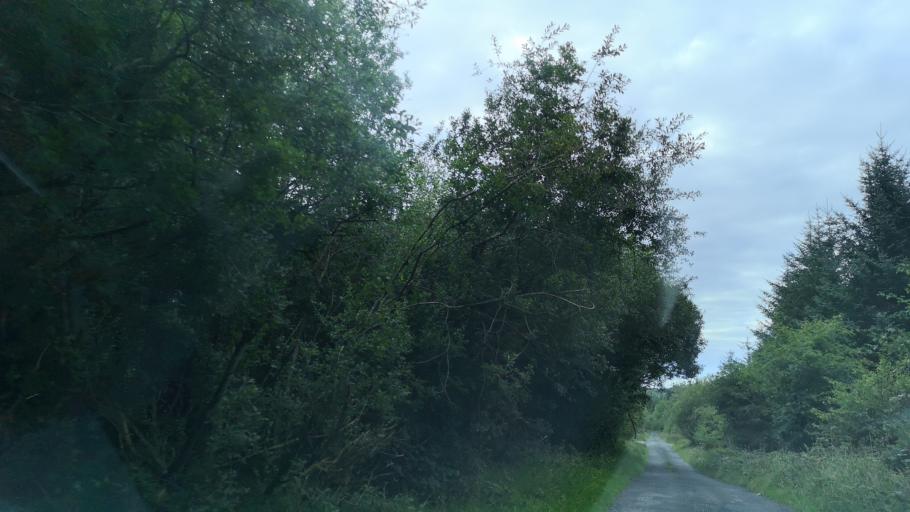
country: IE
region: Connaught
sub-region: County Galway
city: Loughrea
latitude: 53.1351
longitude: -8.5204
